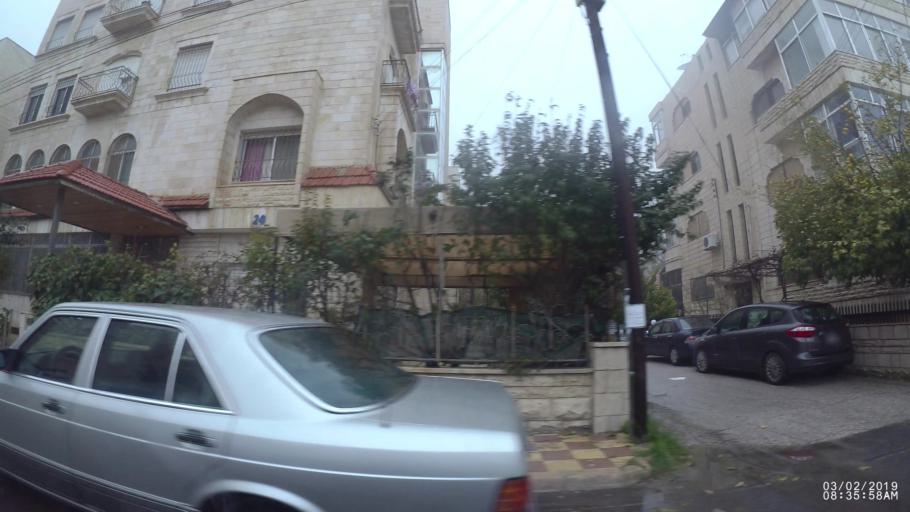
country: JO
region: Amman
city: Wadi as Sir
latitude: 31.9626
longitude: 35.8747
